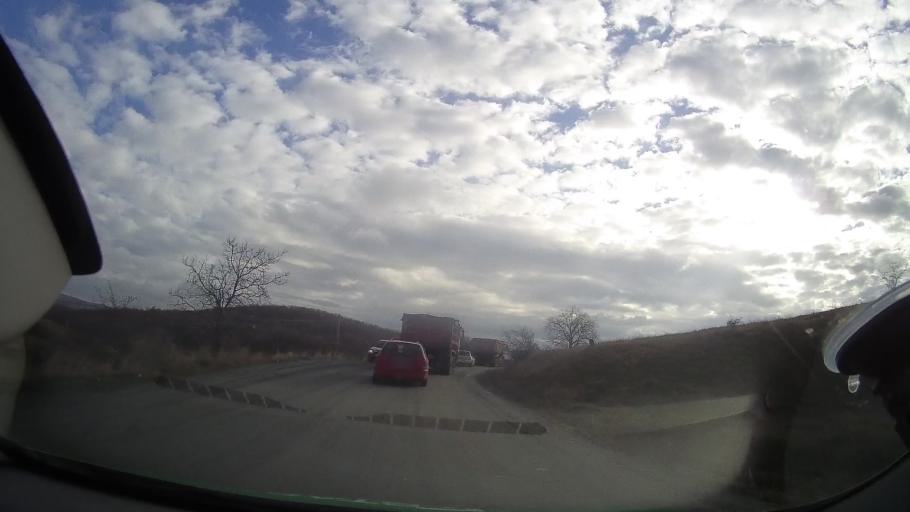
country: RO
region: Cluj
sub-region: Comuna Savadisla
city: Savadisla
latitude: 46.6532
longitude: 23.4546
